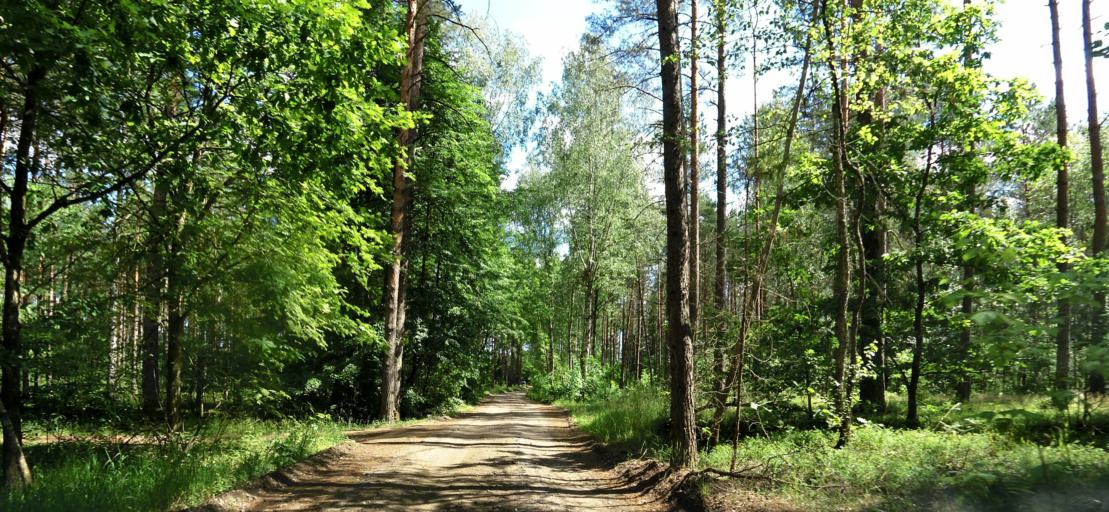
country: LT
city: Nemencine
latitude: 54.8179
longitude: 25.3902
